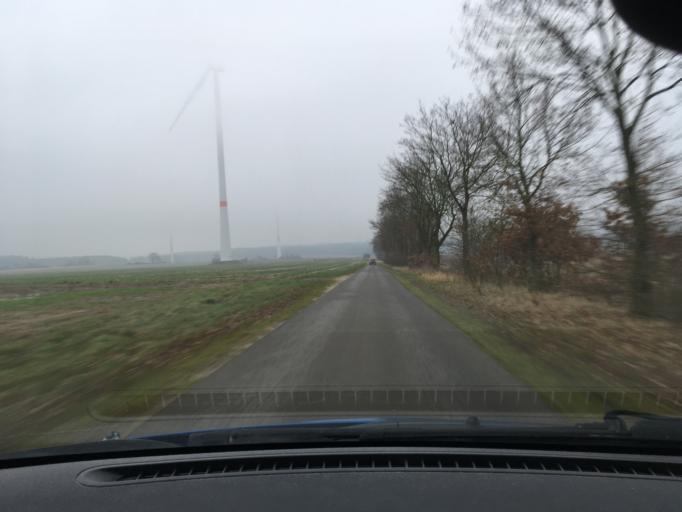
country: DE
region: Lower Saxony
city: Soderstorf
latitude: 53.0914
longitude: 10.1658
